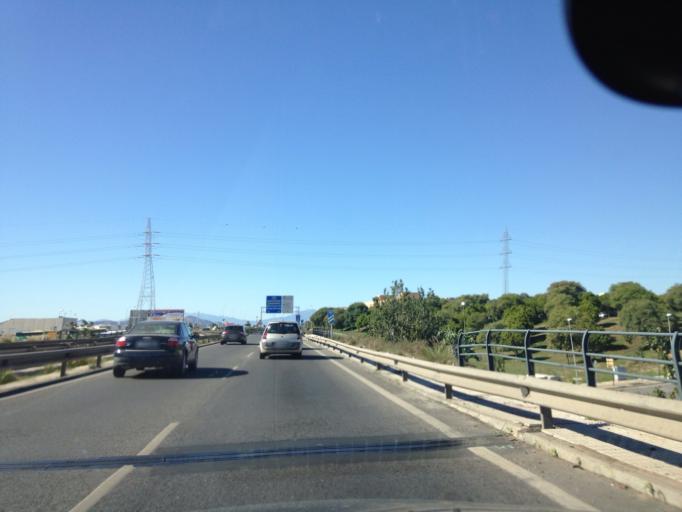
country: ES
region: Andalusia
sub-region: Provincia de Malaga
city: Malaga
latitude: 36.7129
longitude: -4.4660
